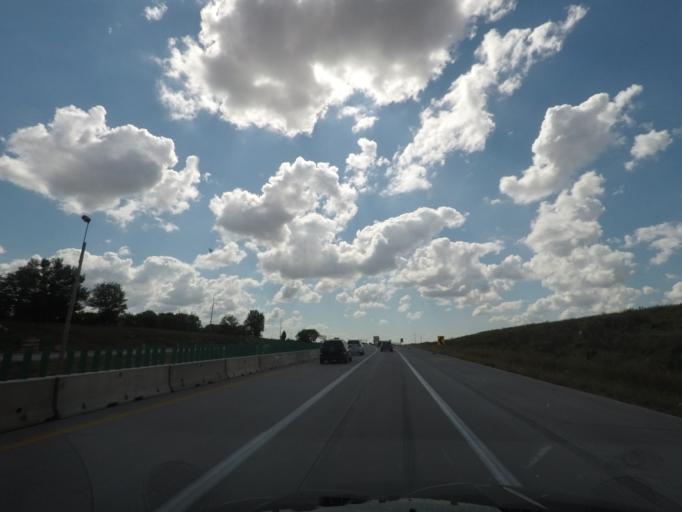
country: US
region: Iowa
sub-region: Story County
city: Huxley
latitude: 41.9534
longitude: -93.5701
